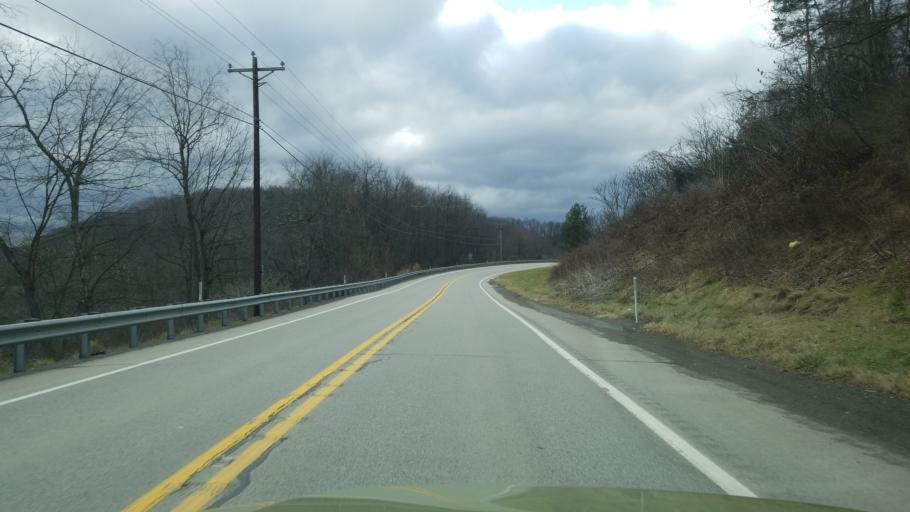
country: US
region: Pennsylvania
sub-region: Indiana County
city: Clymer
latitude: 40.8114
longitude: -79.0520
